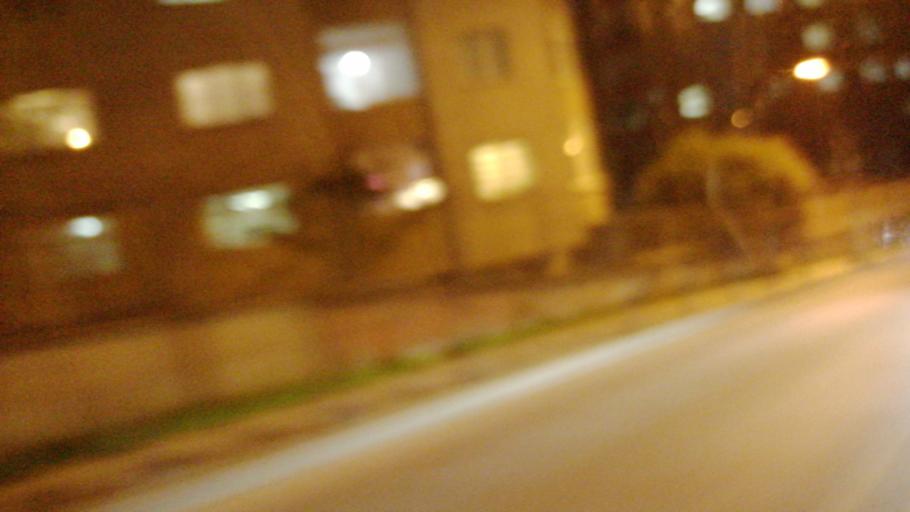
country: TR
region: Istanbul
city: Umraniye
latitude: 40.9999
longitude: 29.1401
